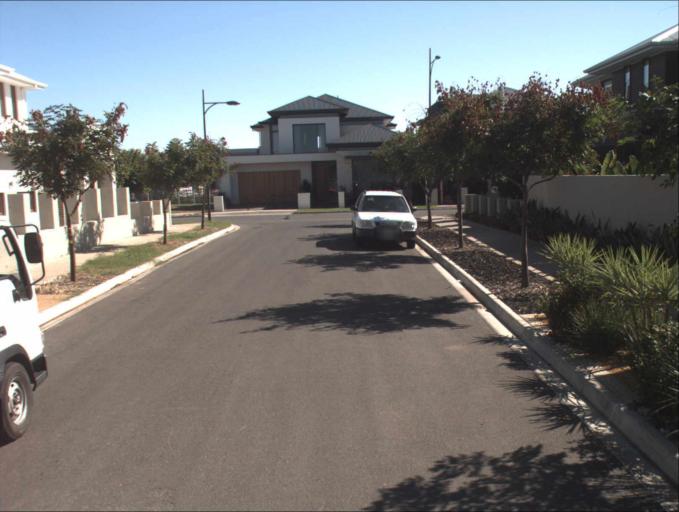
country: AU
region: South Australia
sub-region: Port Adelaide Enfield
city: Klemzig
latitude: -34.8647
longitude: 138.6322
